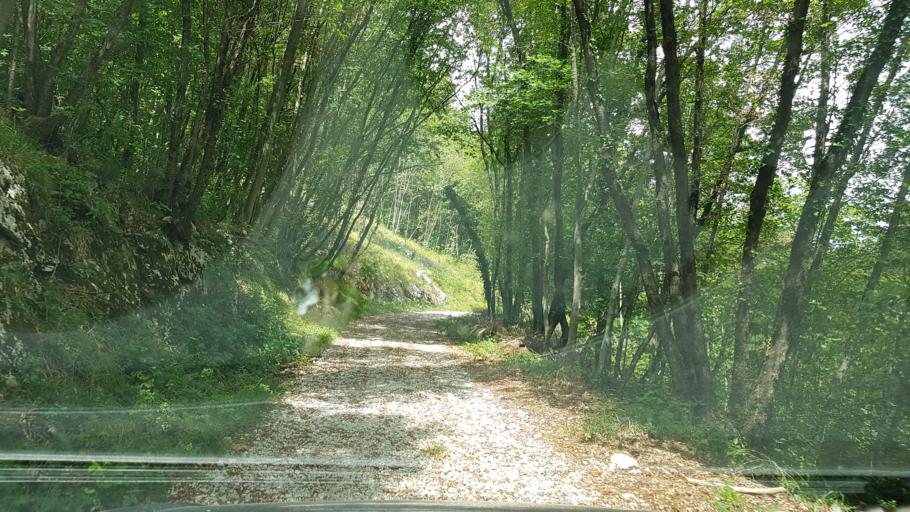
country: SI
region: Nova Gorica
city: Solkan
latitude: 46.0105
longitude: 13.6416
